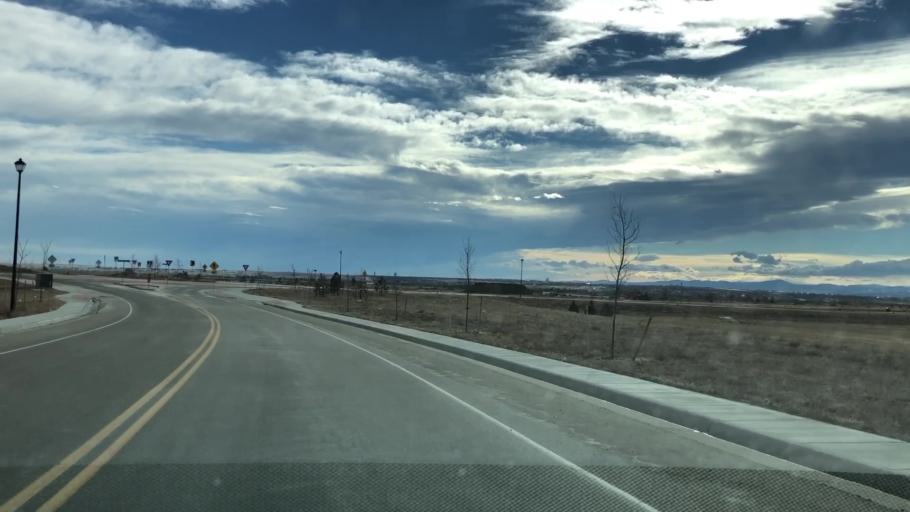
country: US
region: Colorado
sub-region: Weld County
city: Windsor
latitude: 40.5313
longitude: -104.9387
